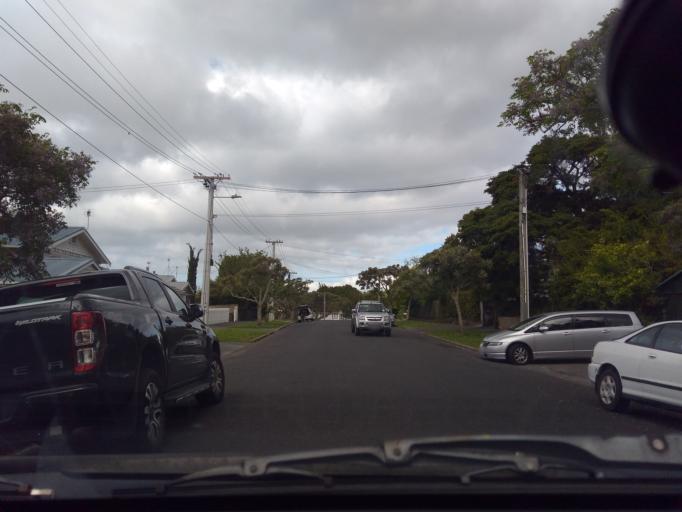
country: NZ
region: Auckland
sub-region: Auckland
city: Rosebank
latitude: -36.8766
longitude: 174.7132
